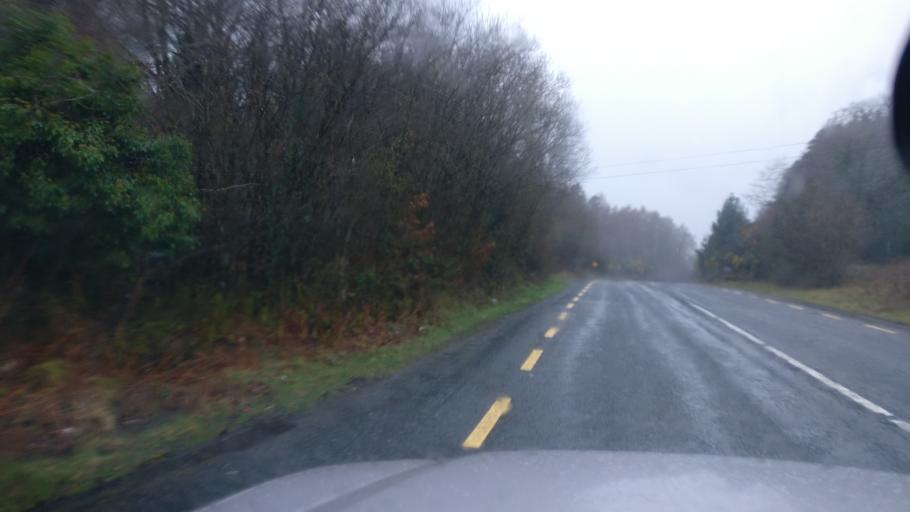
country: IE
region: Connaught
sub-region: County Galway
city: Loughrea
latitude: 53.1433
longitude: -8.4703
